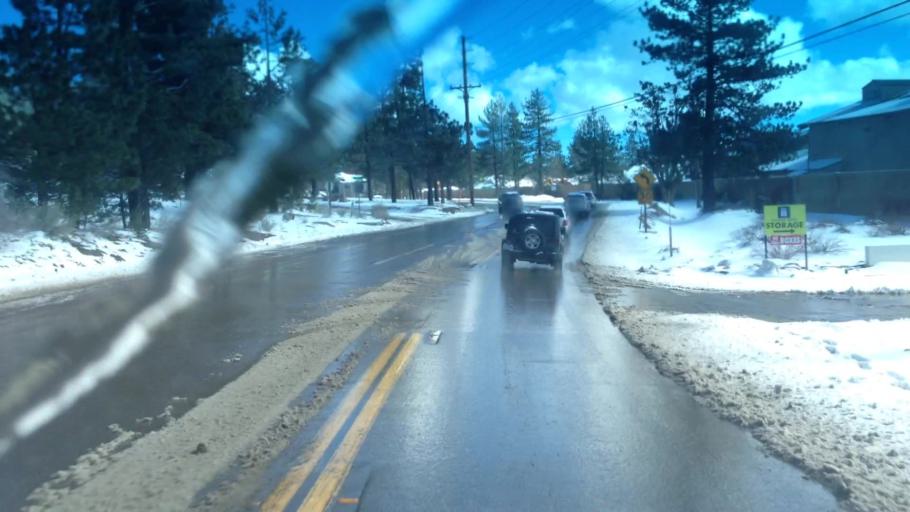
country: US
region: California
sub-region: San Bernardino County
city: Big Bear City
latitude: 34.2661
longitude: -116.8577
